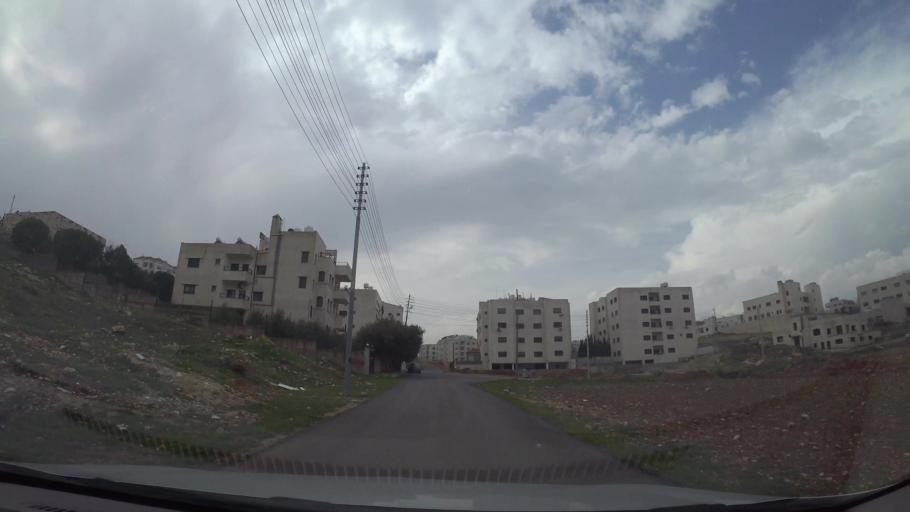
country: JO
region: Amman
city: Umm as Summaq
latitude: 31.8821
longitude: 35.8666
